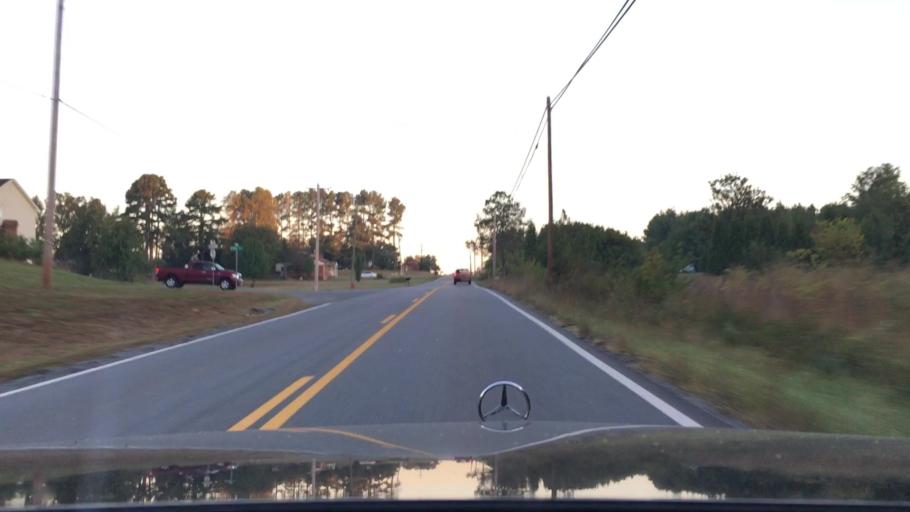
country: US
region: Virginia
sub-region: Campbell County
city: Timberlake
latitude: 37.3067
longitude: -79.2352
